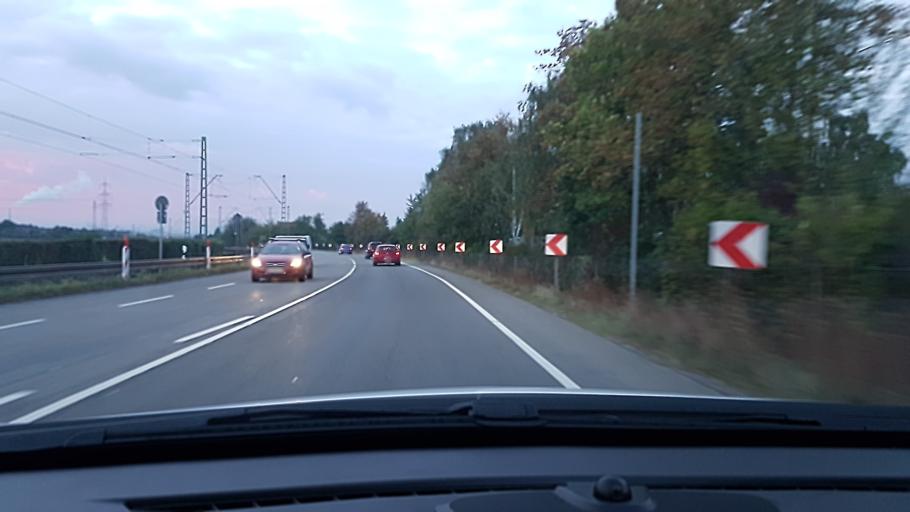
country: DE
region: Hesse
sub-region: Regierungsbezirk Darmstadt
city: Steinbach am Taunus
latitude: 50.1802
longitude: 8.6057
